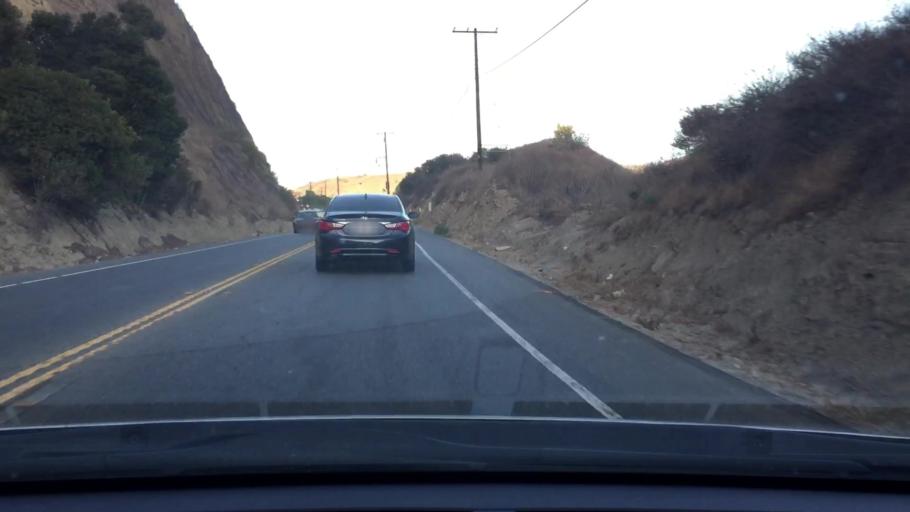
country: US
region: California
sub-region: Orange County
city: Yorba Linda
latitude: 33.9231
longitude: -117.8128
